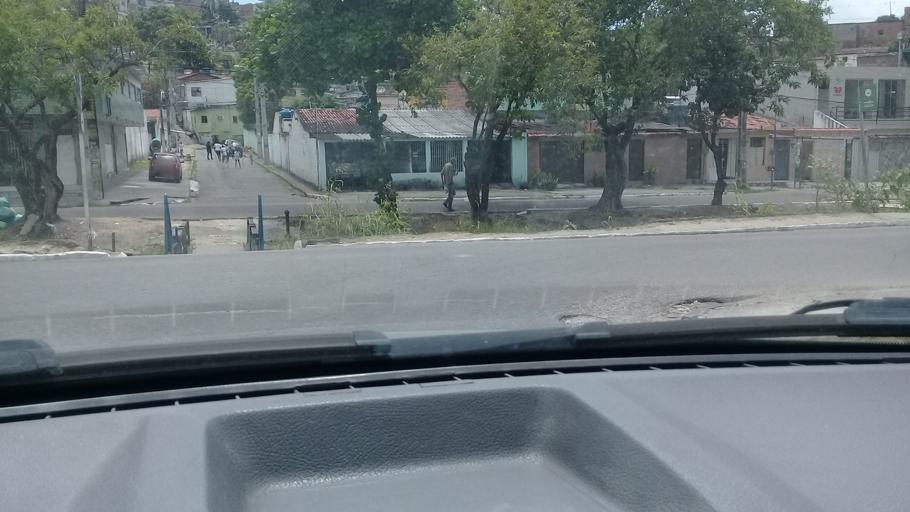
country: BR
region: Pernambuco
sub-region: Jaboatao Dos Guararapes
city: Jaboatao dos Guararapes
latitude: -8.1244
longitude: -34.9505
